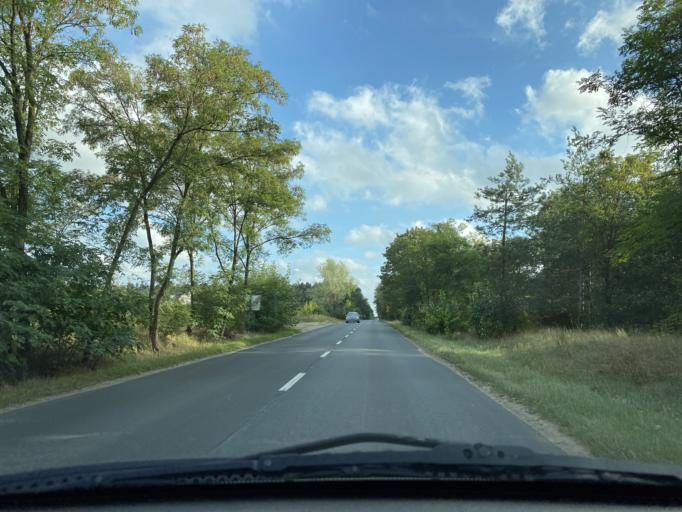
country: PL
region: Greater Poland Voivodeship
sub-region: Powiat poznanski
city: Baranowo
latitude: 52.4144
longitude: 16.7183
